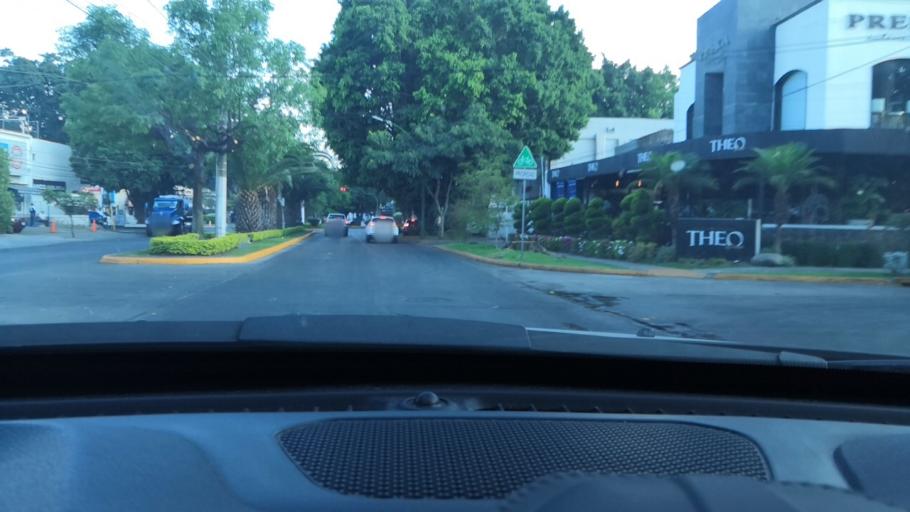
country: MX
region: Jalisco
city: Guadalajara
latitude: 20.6644
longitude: -103.4020
